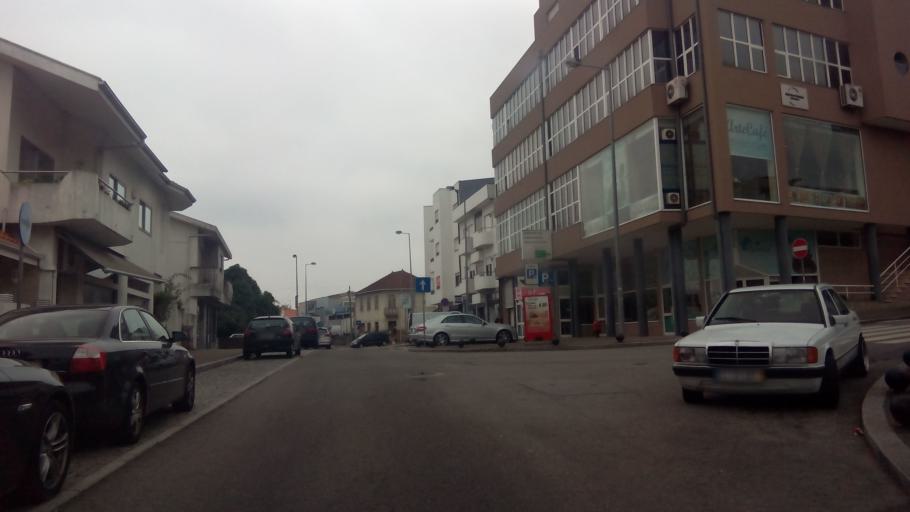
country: PT
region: Porto
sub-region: Paredes
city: Paredes
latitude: 41.2072
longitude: -8.3319
